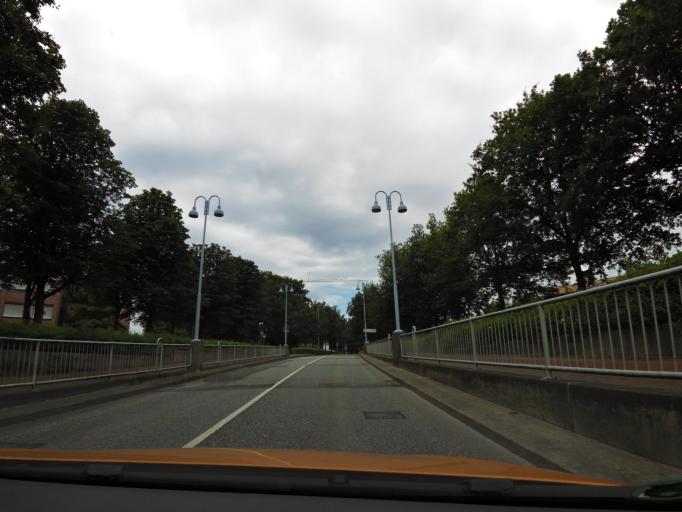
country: DE
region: Lower Saxony
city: Oldenburg
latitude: 53.1530
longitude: 8.1734
